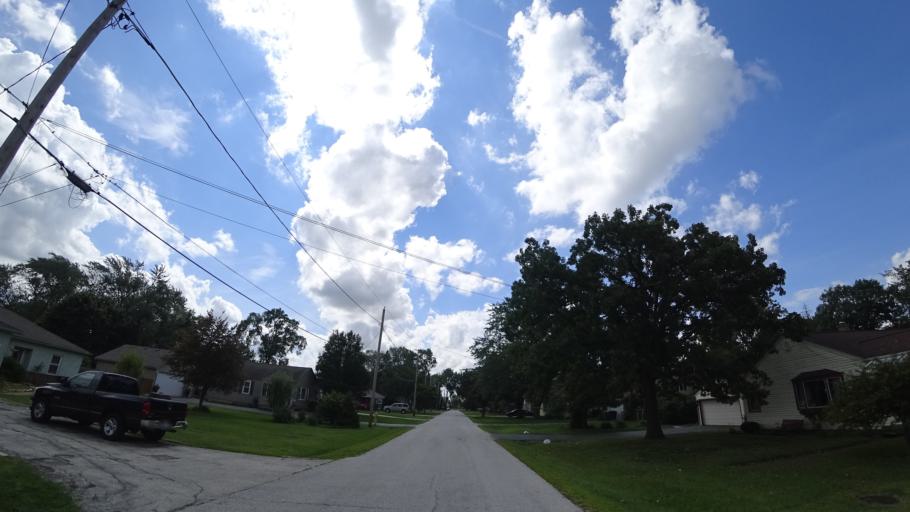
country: US
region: Illinois
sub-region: Cook County
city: Tinley Park
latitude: 41.5688
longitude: -87.7805
